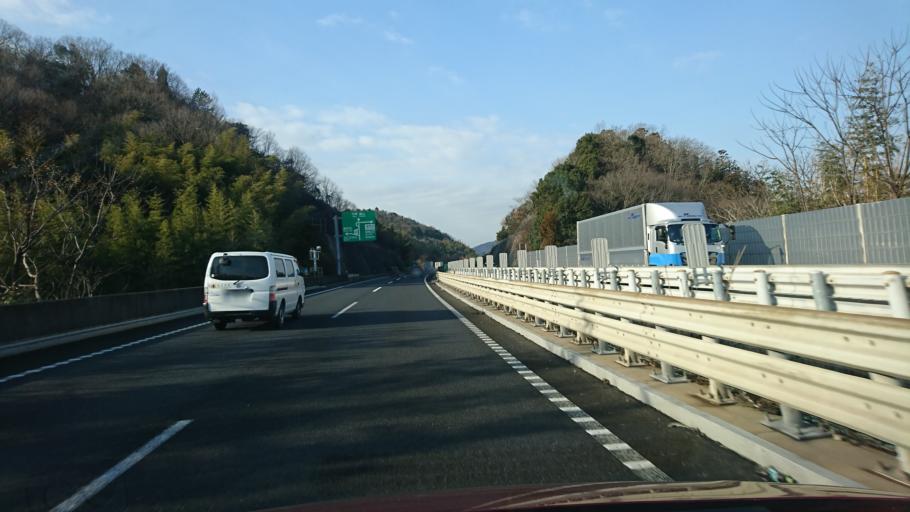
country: JP
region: Hyogo
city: Tatsunocho-tominaga
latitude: 34.8482
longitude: 134.5290
